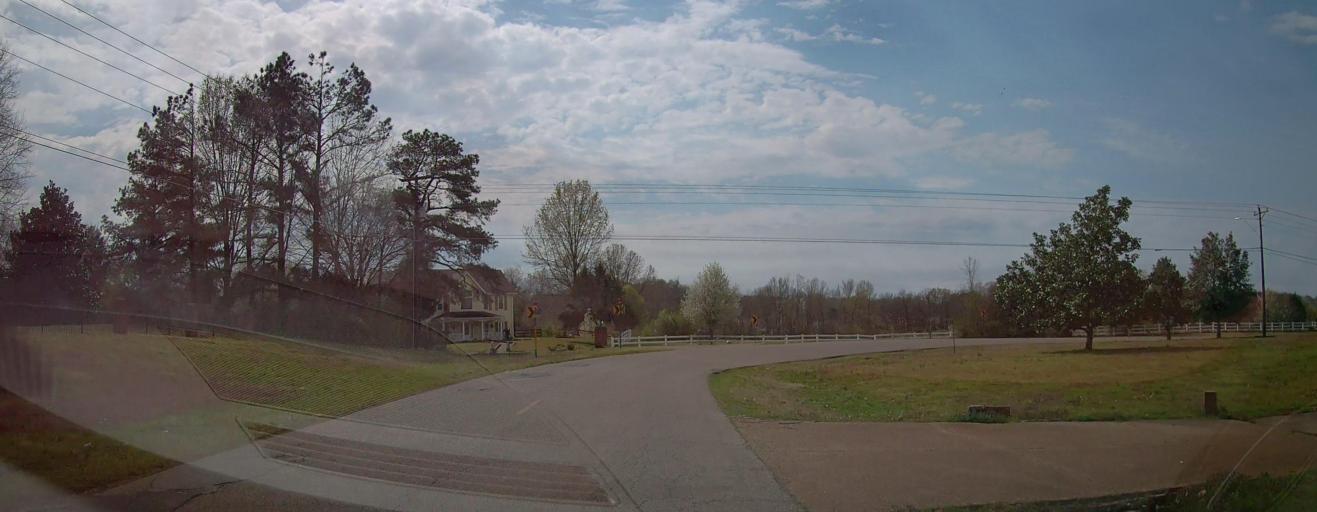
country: US
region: Mississippi
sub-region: De Soto County
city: Olive Branch
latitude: 34.9917
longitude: -89.8484
